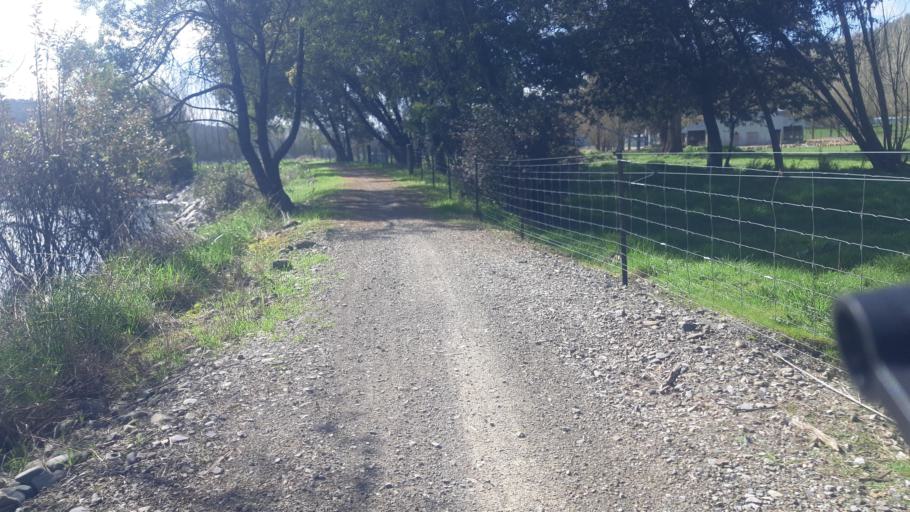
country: NZ
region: Tasman
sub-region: Tasman District
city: Wakefield
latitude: -41.4467
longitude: 172.9753
